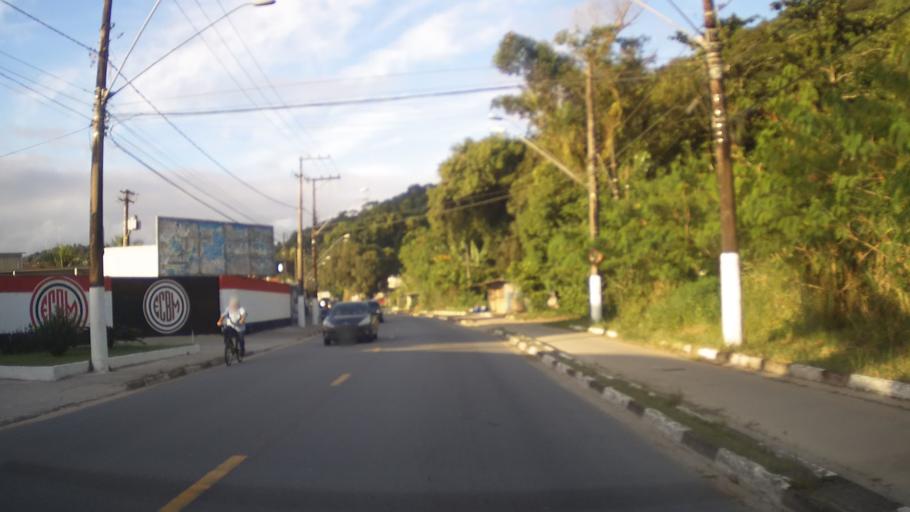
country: BR
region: Sao Paulo
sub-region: Sao Vicente
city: Sao Vicente
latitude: -23.9825
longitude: -46.3926
